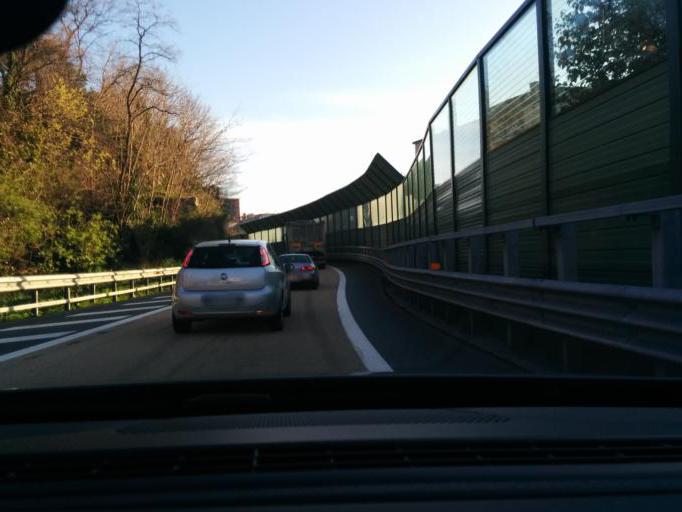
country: IT
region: Liguria
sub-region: Provincia di Genova
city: Genoa
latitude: 44.4491
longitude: 8.8963
